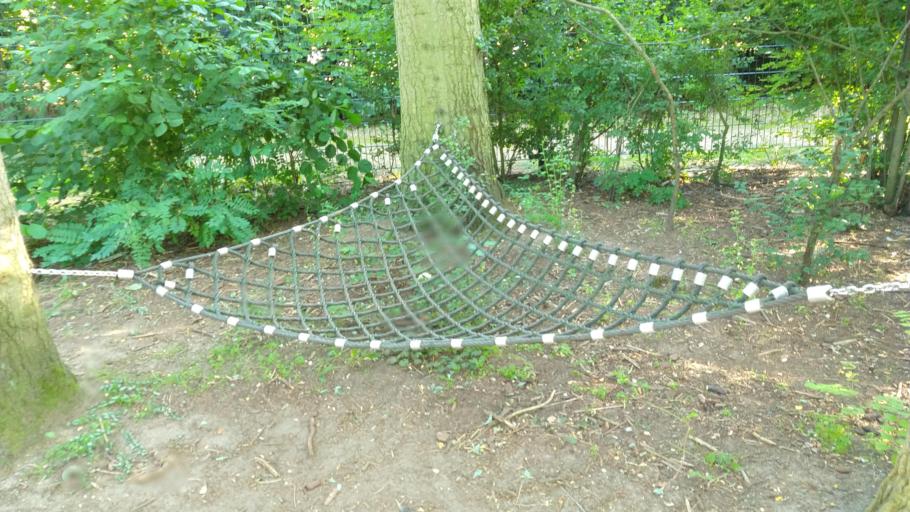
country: NL
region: Gelderland
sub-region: Gemeente Ermelo
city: Ermelo
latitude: 52.2902
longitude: 5.6113
